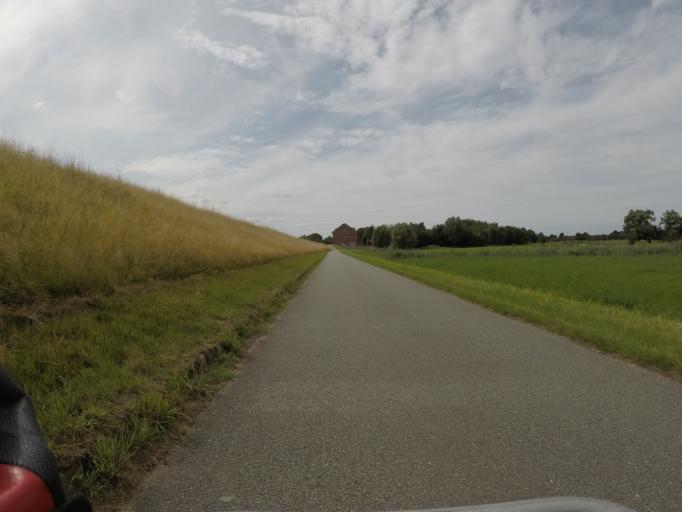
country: DE
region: Lower Saxony
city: Winsen
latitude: 53.3799
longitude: 10.2283
